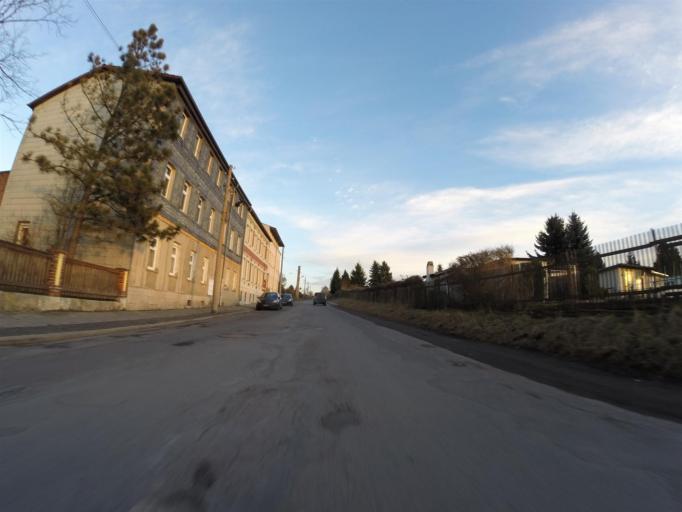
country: DE
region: Thuringia
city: Apolda
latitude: 51.0209
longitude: 11.5263
